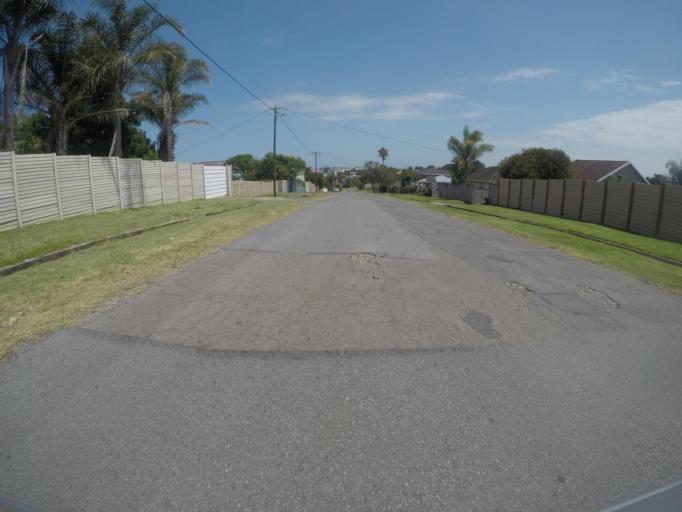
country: ZA
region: Eastern Cape
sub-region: Buffalo City Metropolitan Municipality
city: East London
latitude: -32.9735
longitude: 27.8746
